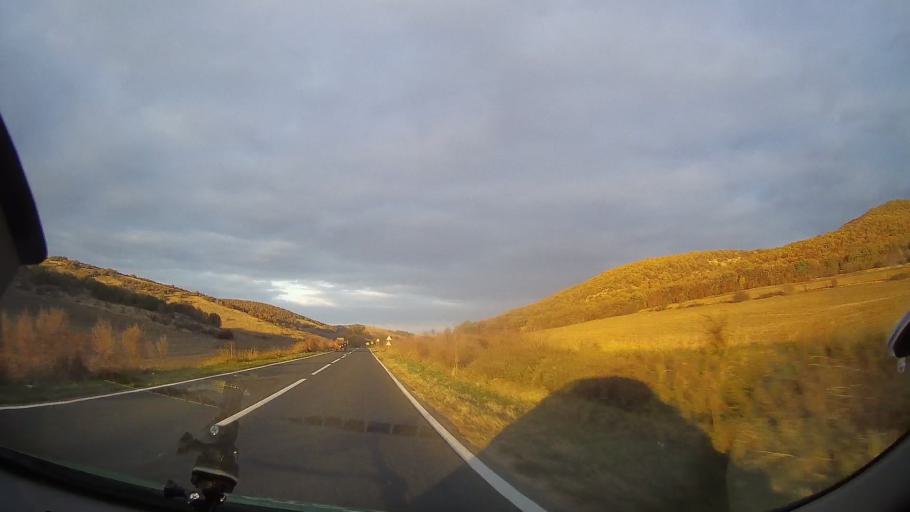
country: RO
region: Tulcea
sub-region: Comuna Ciucurova
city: Ciucurova
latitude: 44.9560
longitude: 28.5156
